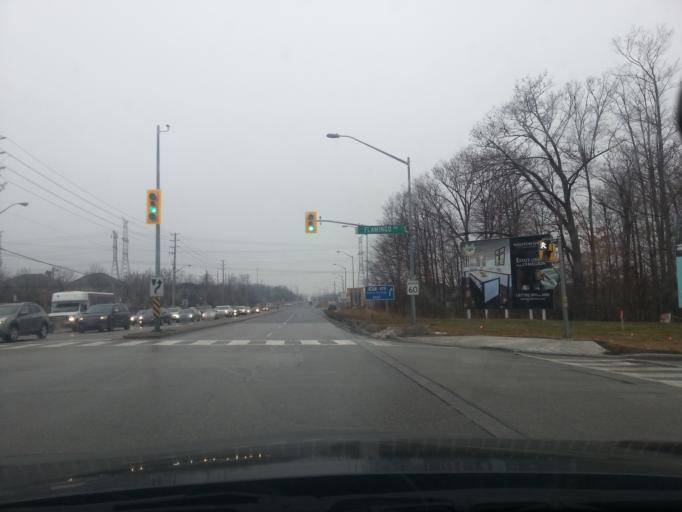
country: CA
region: Ontario
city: Concord
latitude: 43.8223
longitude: -79.4527
